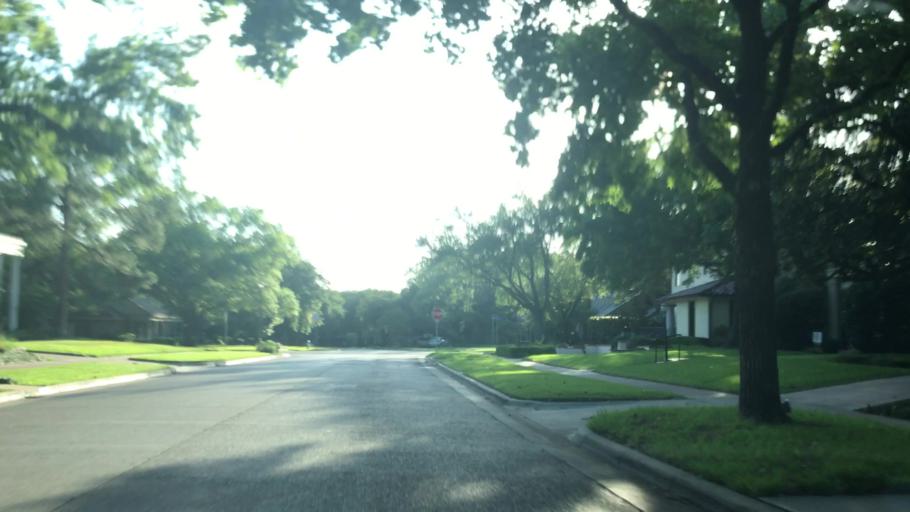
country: US
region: Texas
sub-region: Dallas County
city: University Park
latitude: 32.8323
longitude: -96.8184
